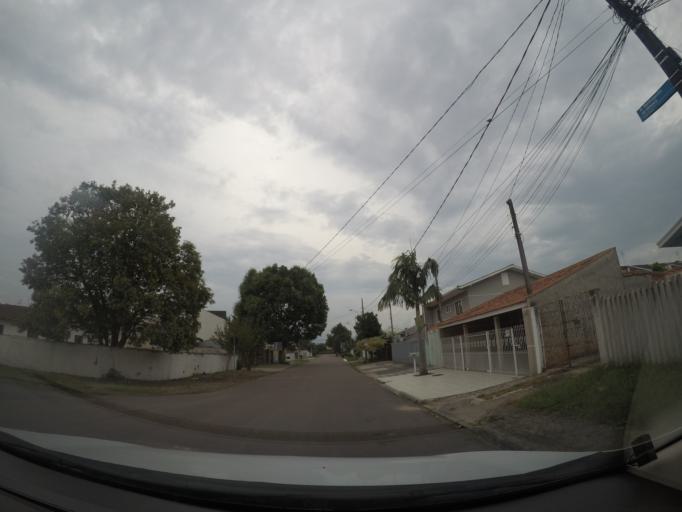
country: BR
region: Parana
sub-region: Curitiba
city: Curitiba
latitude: -25.4713
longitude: -49.2434
